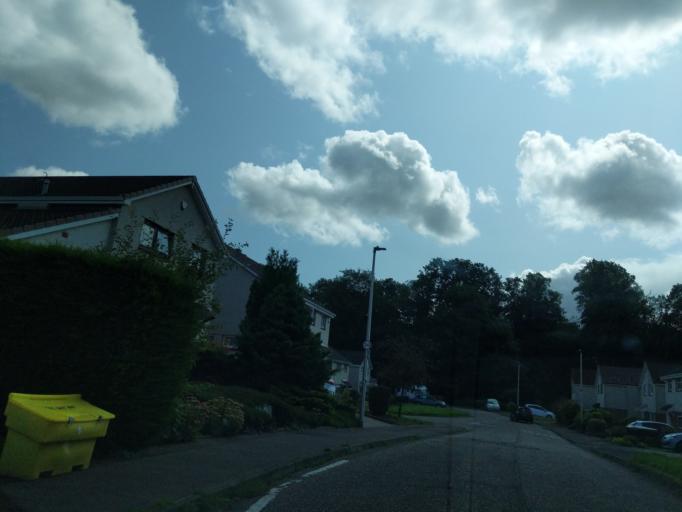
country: GB
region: Scotland
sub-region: Edinburgh
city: Currie
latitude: 55.9094
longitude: -3.2944
